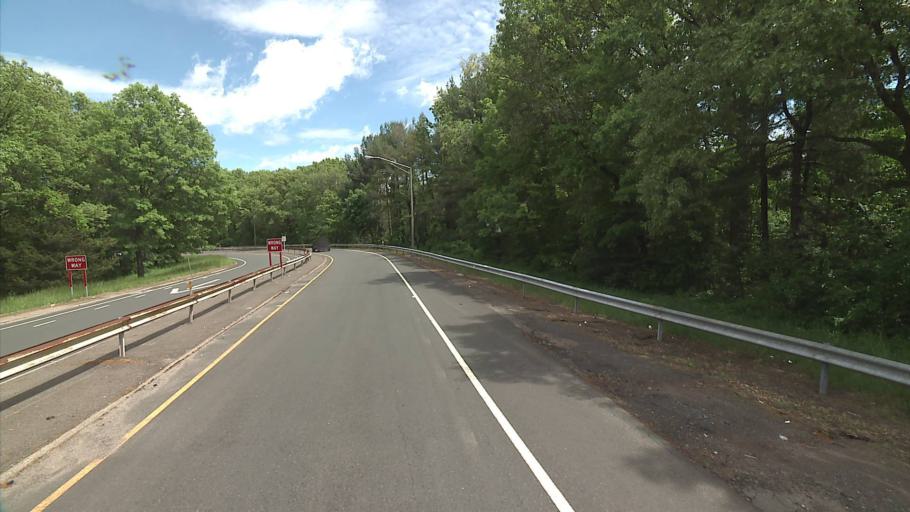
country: US
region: Connecticut
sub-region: New Haven County
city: North Haven
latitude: 41.3983
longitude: -72.8513
